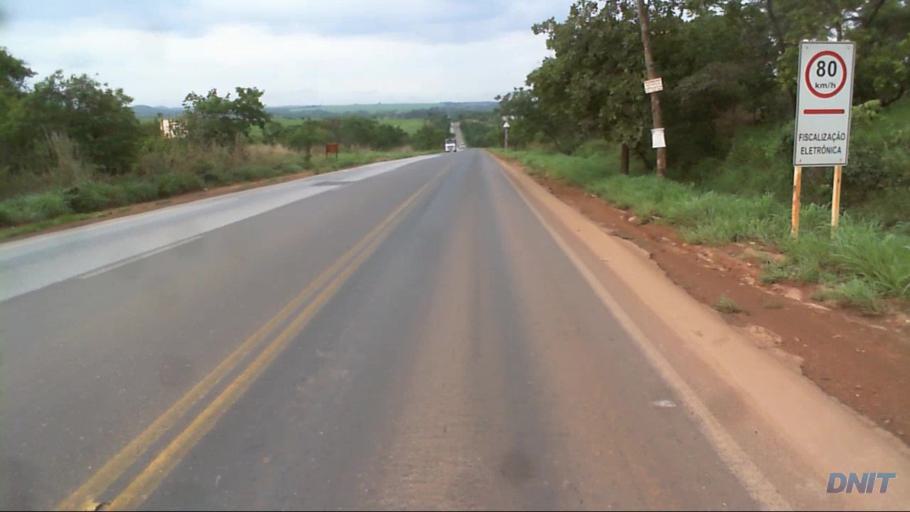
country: BR
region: Goias
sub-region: Uruacu
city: Uruacu
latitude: -14.5744
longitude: -49.1577
